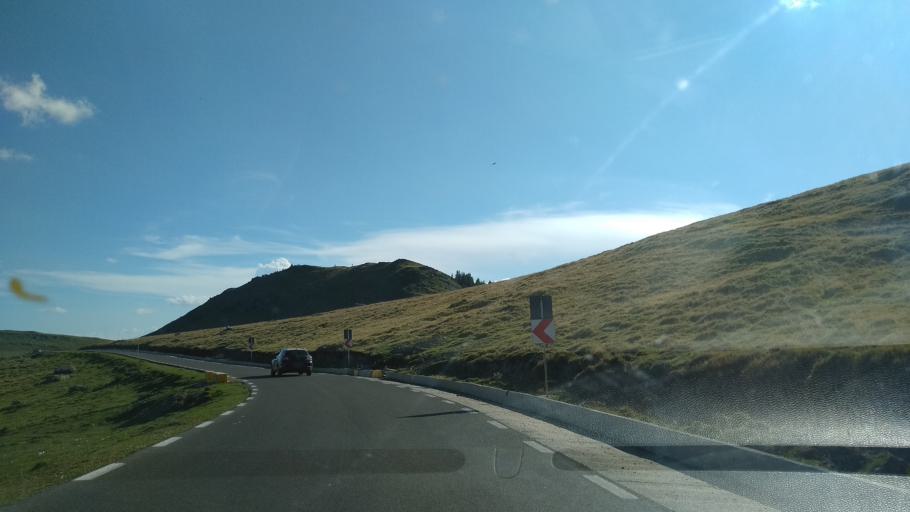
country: RO
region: Prahova
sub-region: Oras Busteni
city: Busteni
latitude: 45.3640
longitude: 25.4592
